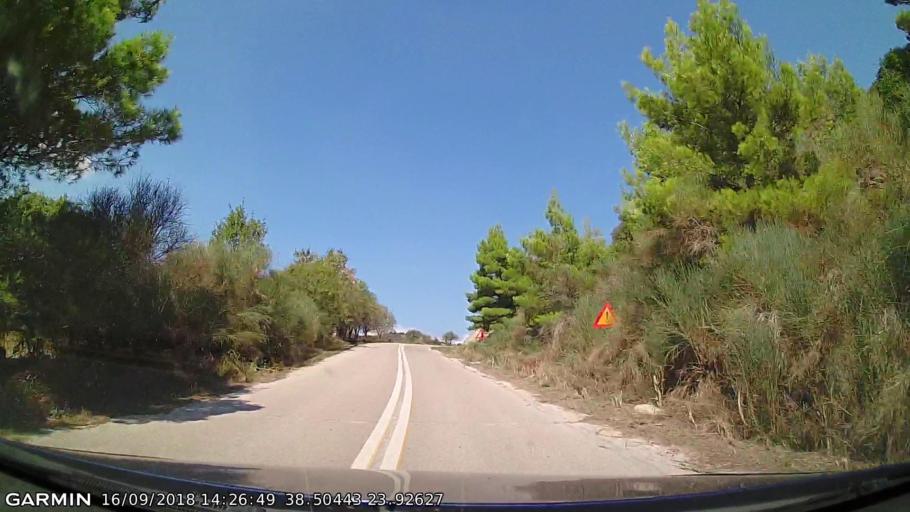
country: GR
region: Central Greece
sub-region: Nomos Evvoias
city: Yimnon
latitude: 38.5046
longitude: 23.9263
